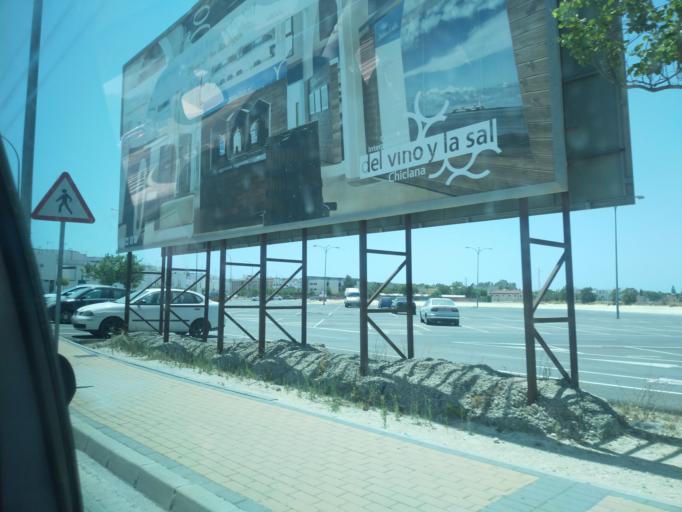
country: ES
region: Andalusia
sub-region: Provincia de Cadiz
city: Chiclana de la Frontera
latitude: 36.4229
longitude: -6.1544
